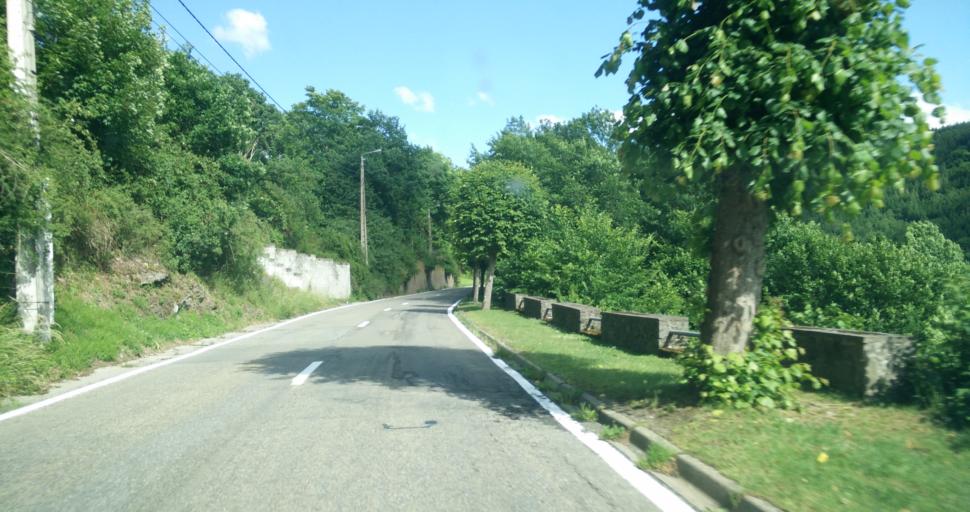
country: BE
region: Wallonia
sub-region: Province du Luxembourg
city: La Roche-en-Ardenne
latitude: 50.1767
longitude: 5.5882
